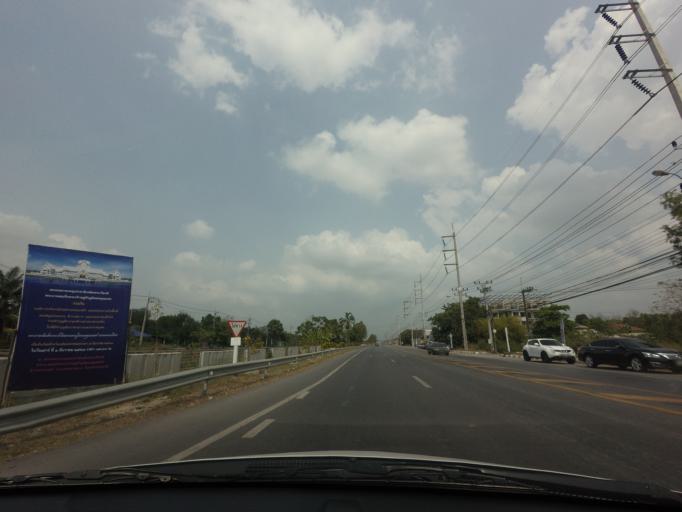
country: TH
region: Pathum Thani
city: Thanyaburi
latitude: 14.0598
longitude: 100.7102
